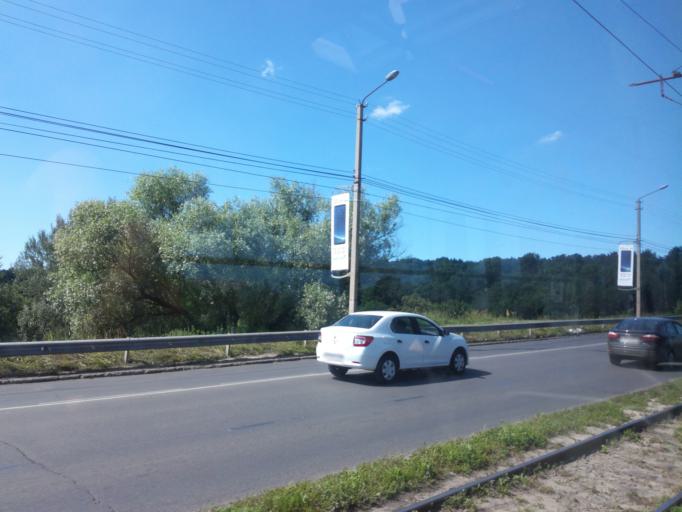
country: RU
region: Kursk
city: Kursk
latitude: 51.7489
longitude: 36.1730
